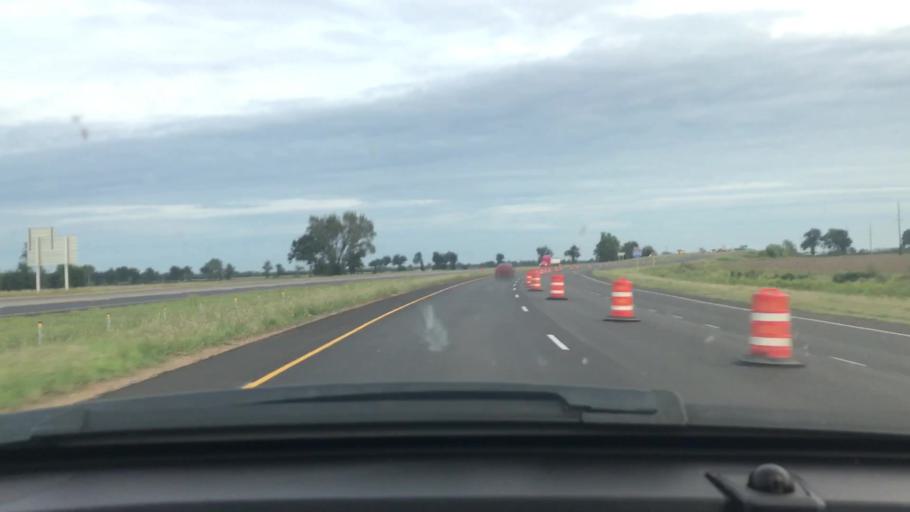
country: US
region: Arkansas
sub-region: Poinsett County
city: Trumann
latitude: 35.6265
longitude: -90.4975
